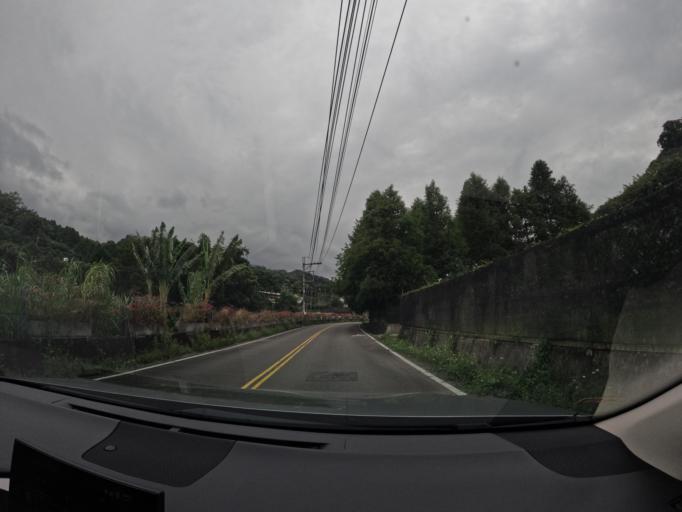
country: TW
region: Taiwan
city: Fengyuan
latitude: 24.3401
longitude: 120.8733
